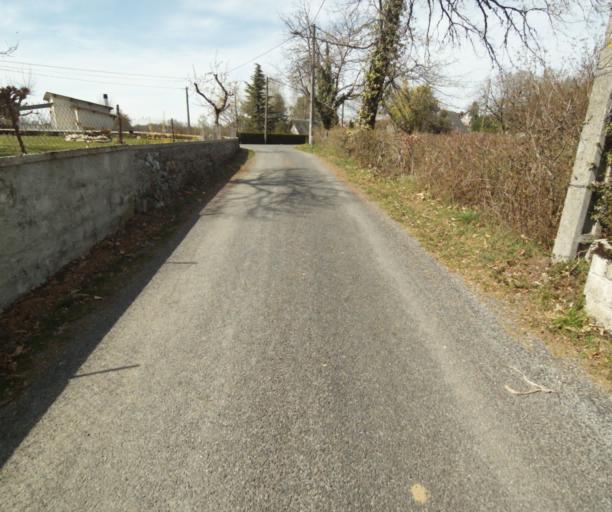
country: FR
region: Limousin
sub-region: Departement de la Correze
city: Seilhac
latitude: 45.3916
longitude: 1.7701
